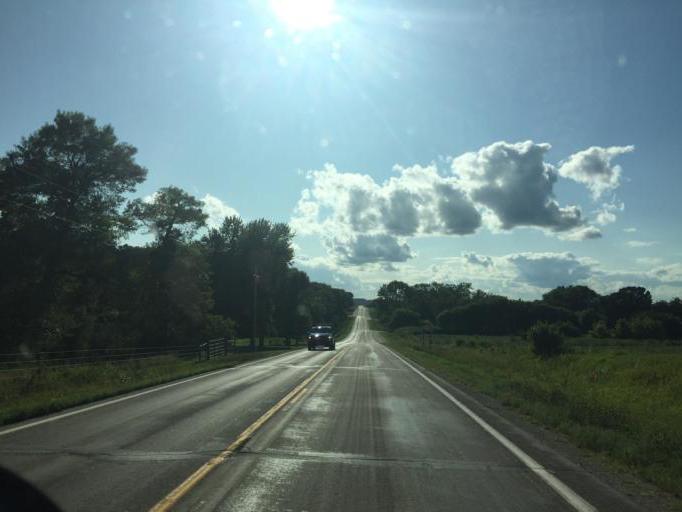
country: US
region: Minnesota
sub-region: Olmsted County
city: Rochester
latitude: 43.9640
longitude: -92.5355
